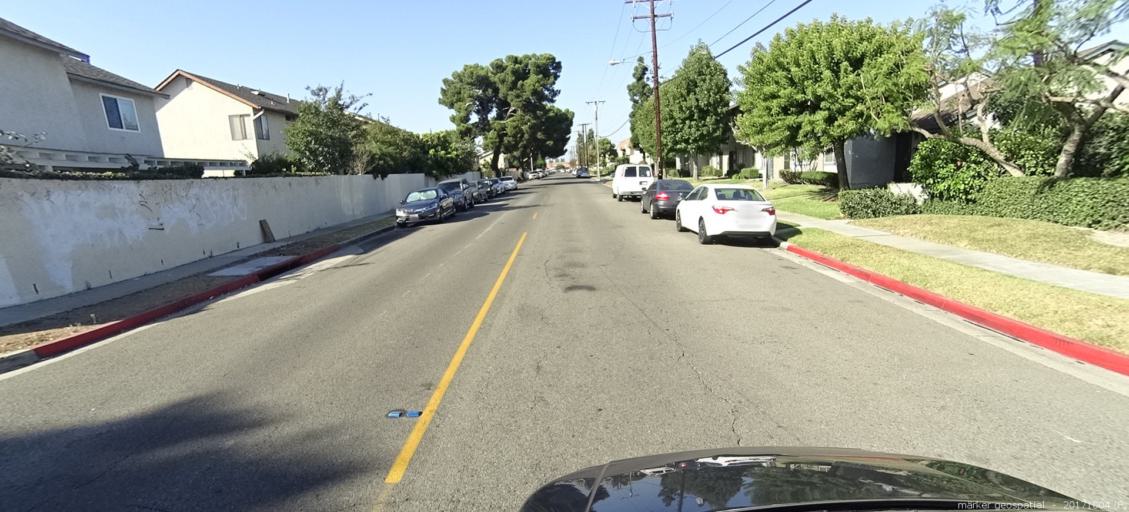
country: US
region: California
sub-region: Orange County
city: Midway City
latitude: 33.7701
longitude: -117.9768
